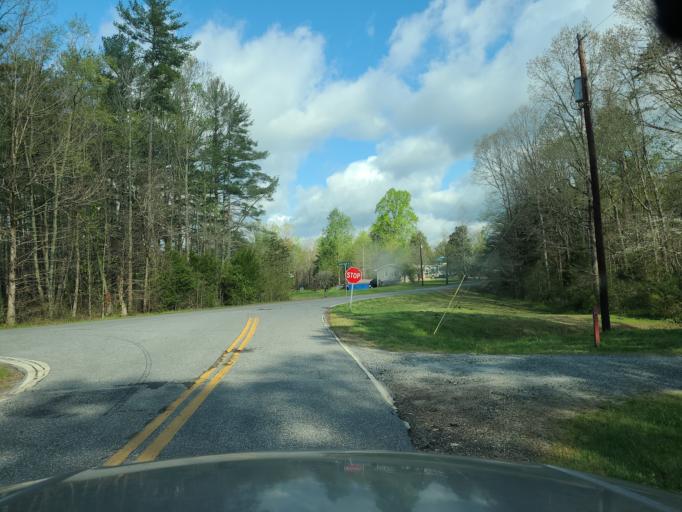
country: US
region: North Carolina
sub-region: Rutherford County
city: Forest City
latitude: 35.4302
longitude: -81.8309
